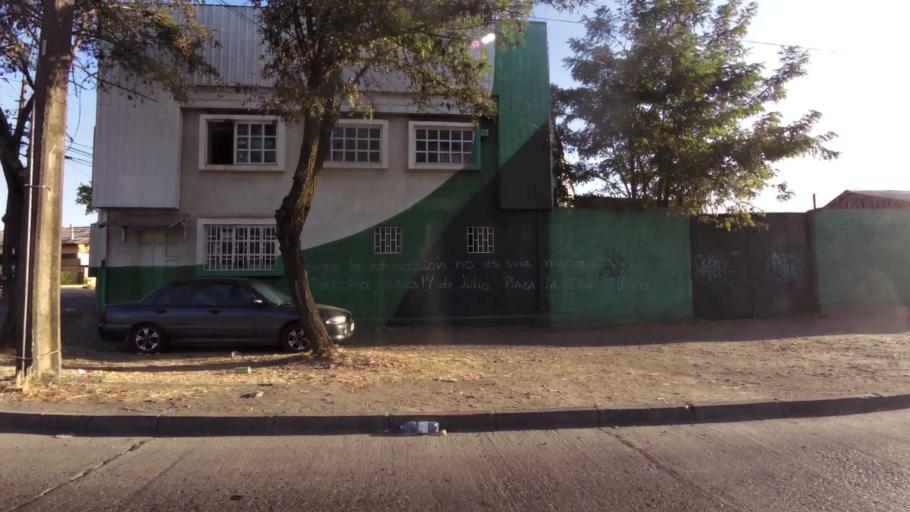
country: CL
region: Maule
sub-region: Provincia de Talca
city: Talca
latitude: -35.4321
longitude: -71.6410
